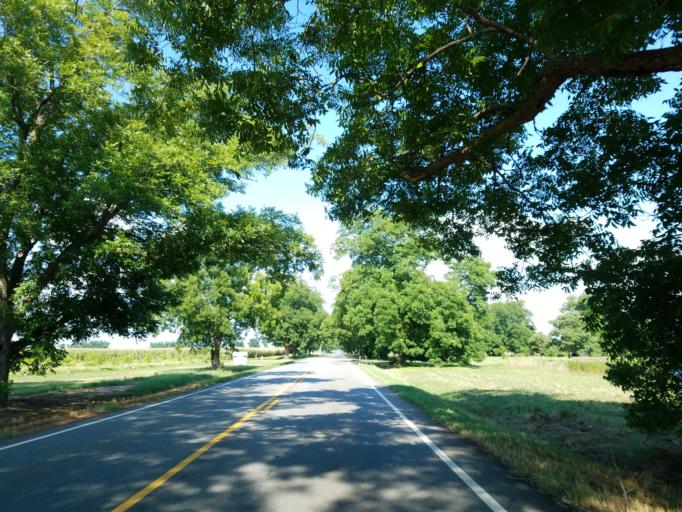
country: US
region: Georgia
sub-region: Peach County
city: Fort Valley
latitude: 32.5539
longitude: -83.8146
